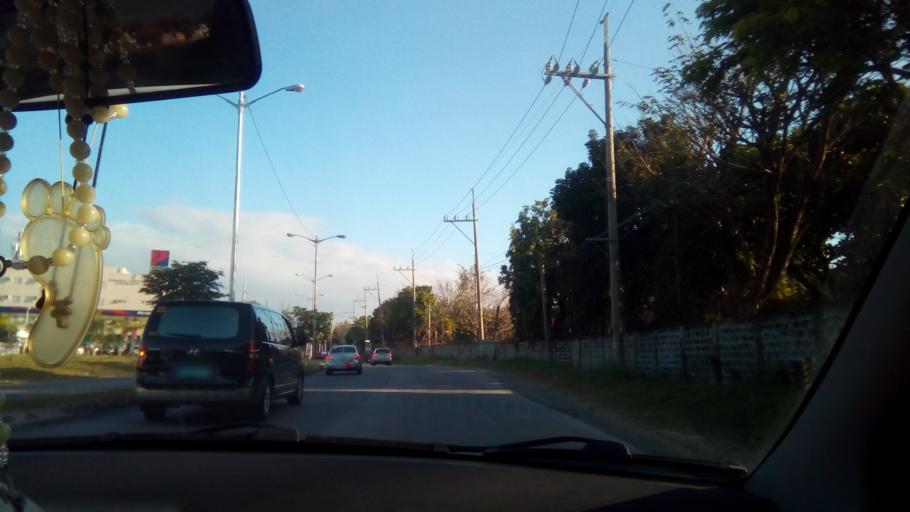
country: PH
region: Calabarzon
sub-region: Province of Laguna
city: San Pedro
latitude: 14.3982
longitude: 121.0116
